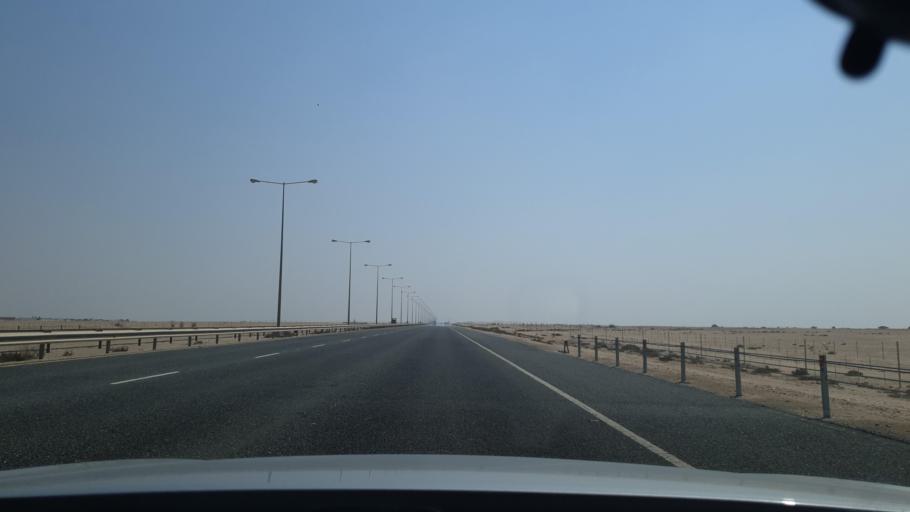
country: QA
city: Al Ghuwayriyah
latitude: 25.8075
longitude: 51.3767
